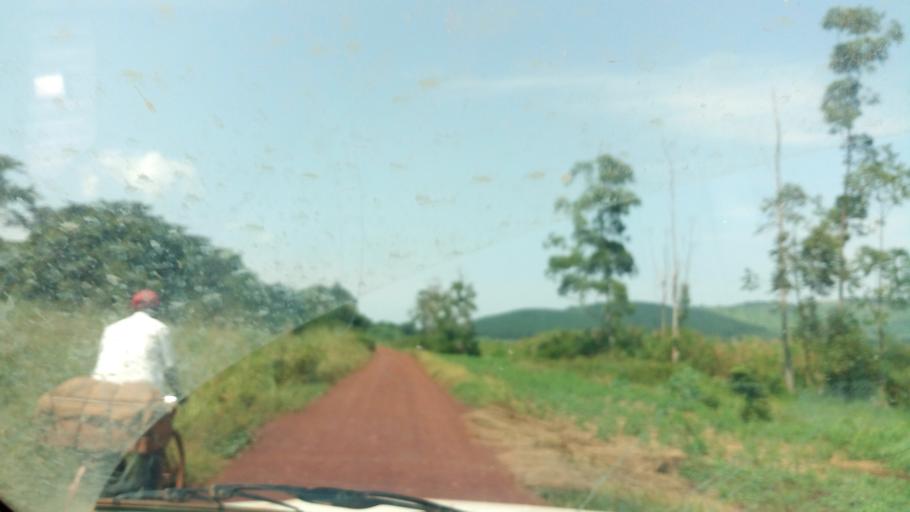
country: UG
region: Western Region
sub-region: Masindi District
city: Masindi
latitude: 1.6577
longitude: 31.8097
